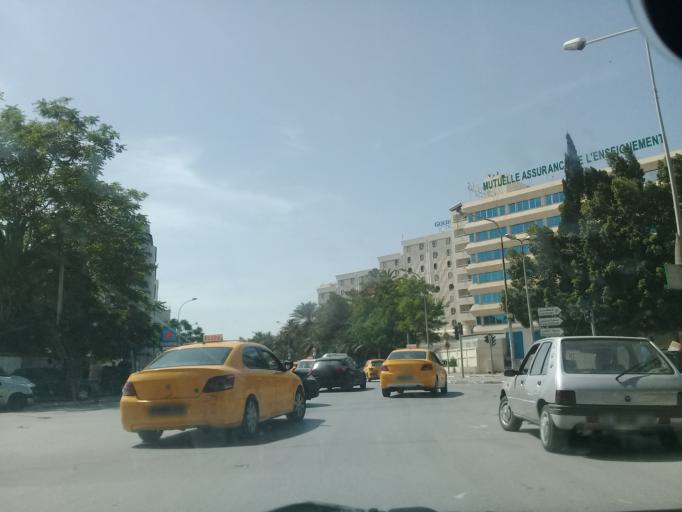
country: TN
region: Tunis
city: Tunis
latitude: 36.8125
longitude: 10.1747
